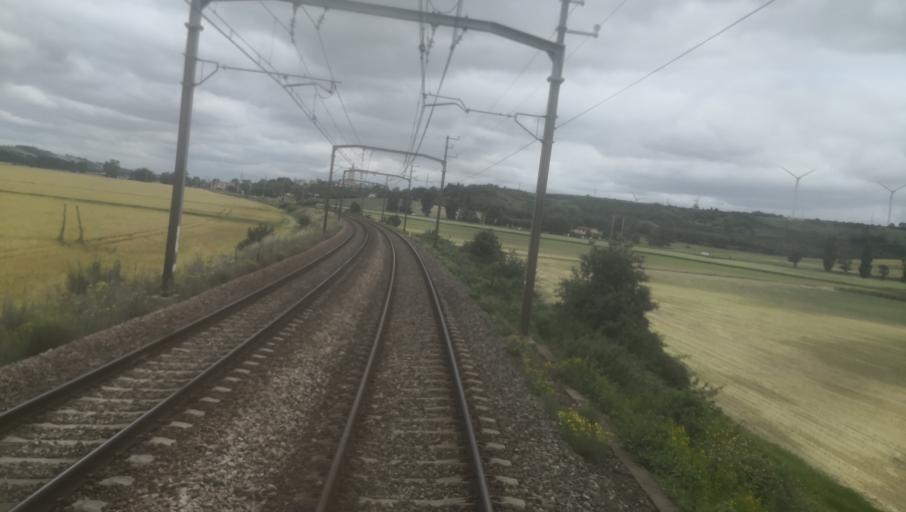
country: FR
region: Midi-Pyrenees
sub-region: Departement de la Haute-Garonne
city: Avignonet-Lauragais
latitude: 43.3594
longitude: 1.8031
